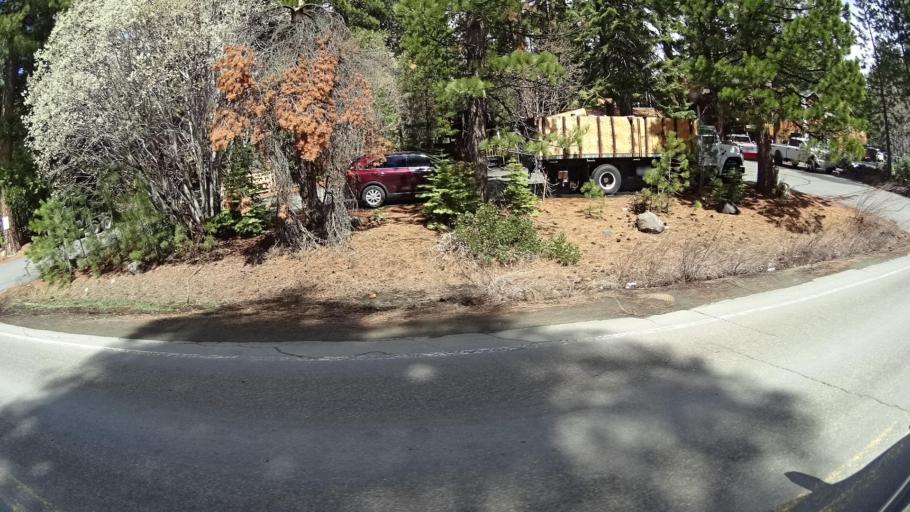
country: US
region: Nevada
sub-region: Washoe County
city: Incline Village
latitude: 39.2528
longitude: -119.9546
